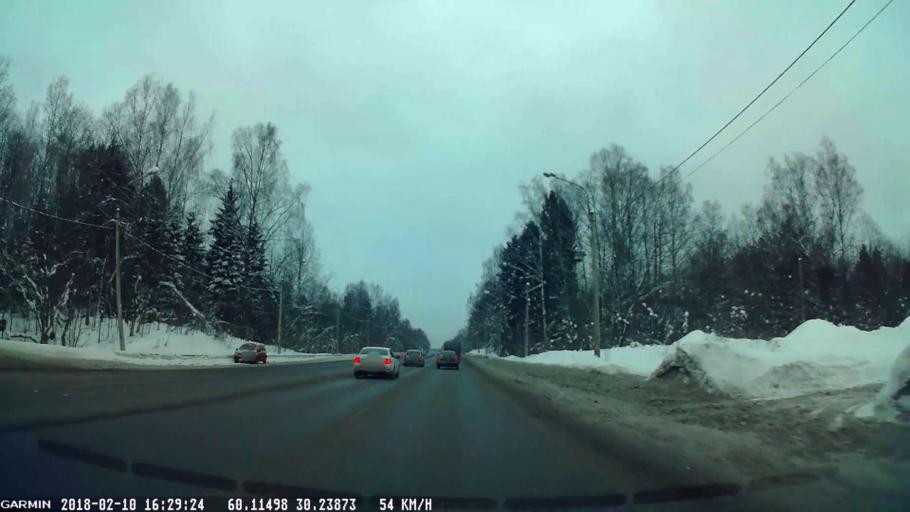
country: RU
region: St.-Petersburg
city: Levashovo
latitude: 60.1154
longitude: 30.2384
